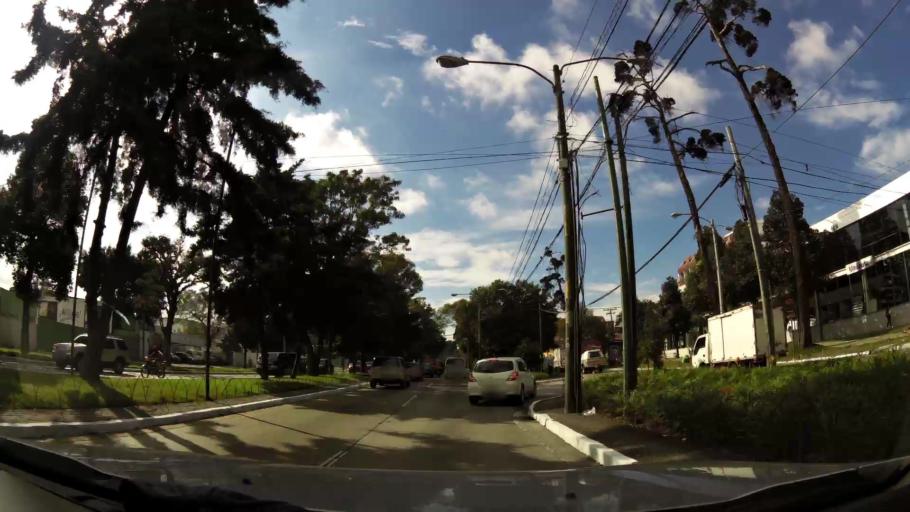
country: GT
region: Guatemala
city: Guatemala City
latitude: 14.6114
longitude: -90.5145
